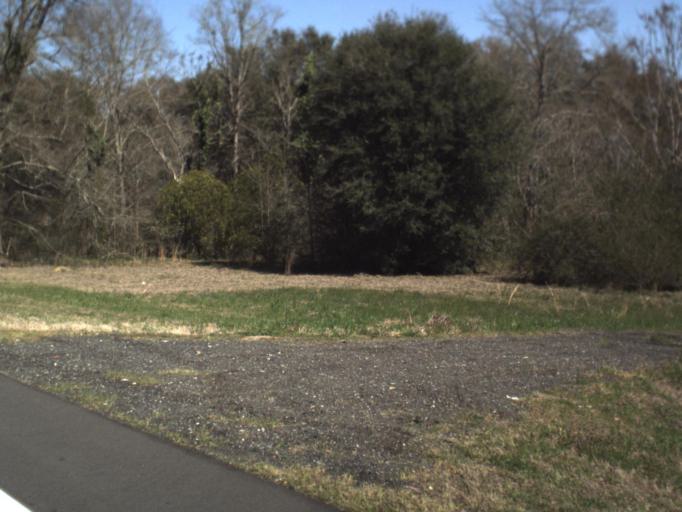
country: US
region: Florida
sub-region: Jackson County
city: Sneads
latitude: 30.7662
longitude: -85.0192
